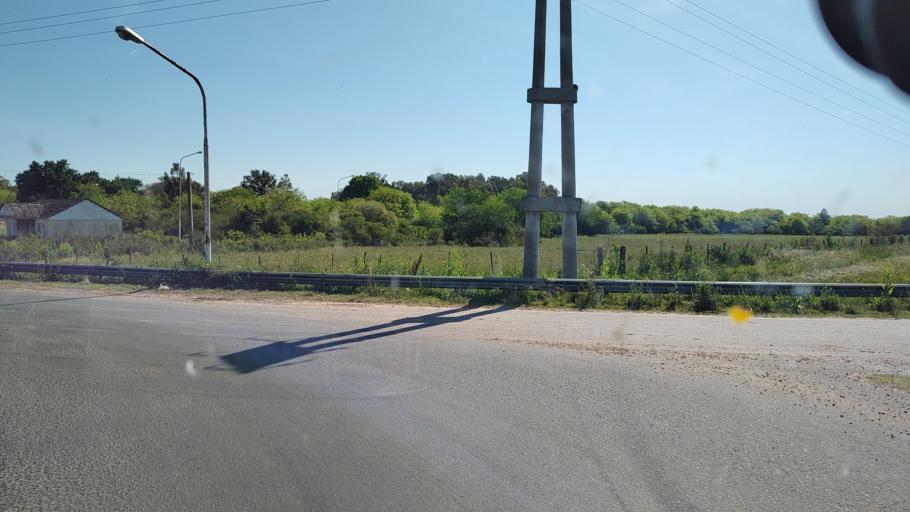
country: AR
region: Entre Rios
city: Colonia Elia
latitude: -32.6642
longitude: -58.4419
